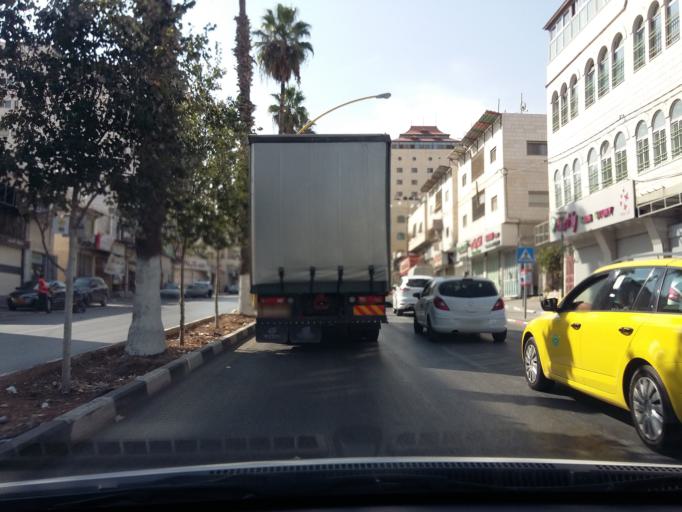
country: PS
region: West Bank
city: Halhul
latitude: 31.5594
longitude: 35.1002
